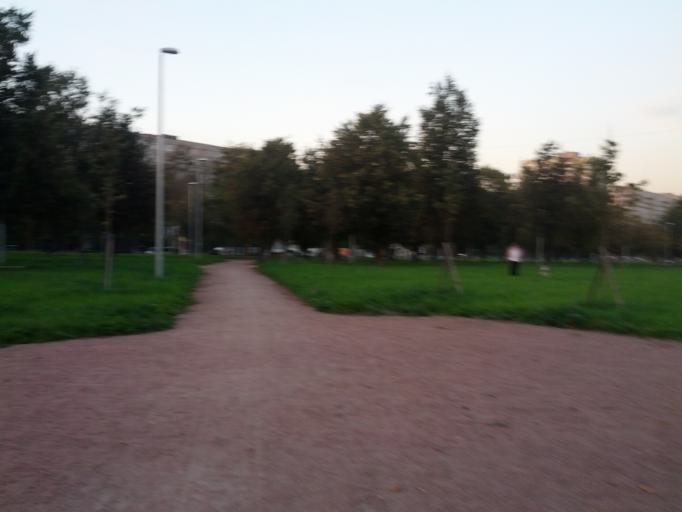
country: RU
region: St.-Petersburg
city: Obukhovo
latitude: 59.8959
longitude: 30.4685
